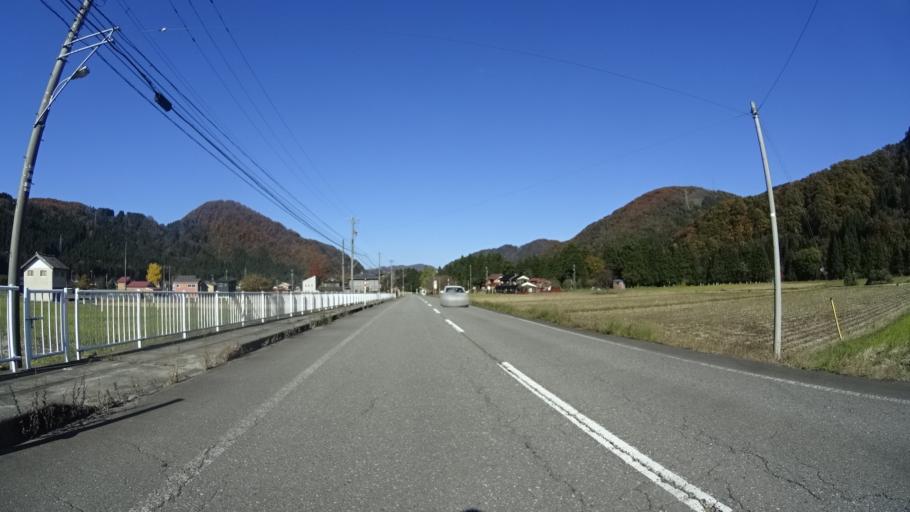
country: JP
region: Ishikawa
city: Tsurugi-asahimachi
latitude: 36.3420
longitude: 136.6312
